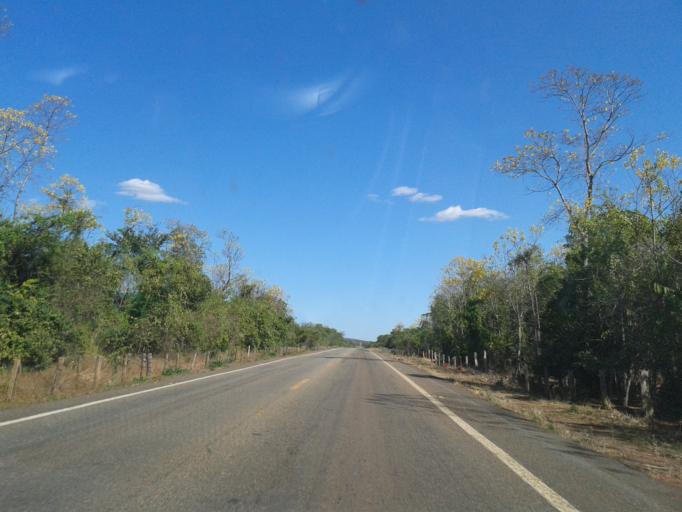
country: BR
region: Goias
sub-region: Crixas
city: Crixas
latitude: -14.0466
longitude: -50.3296
